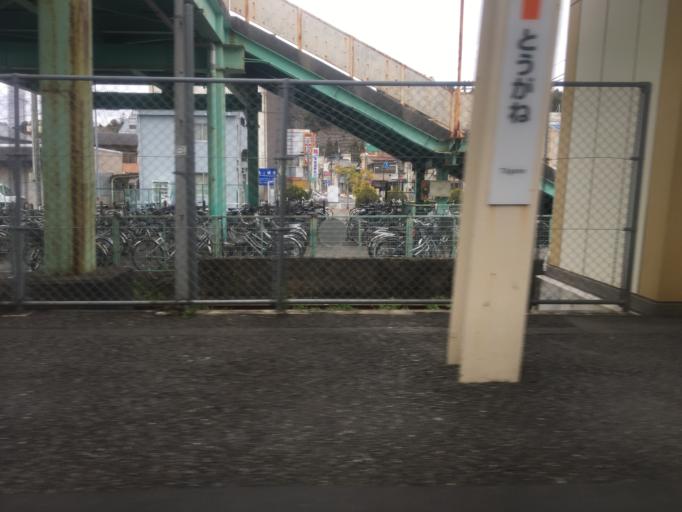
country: JP
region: Chiba
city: Togane
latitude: 35.5600
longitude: 140.3634
